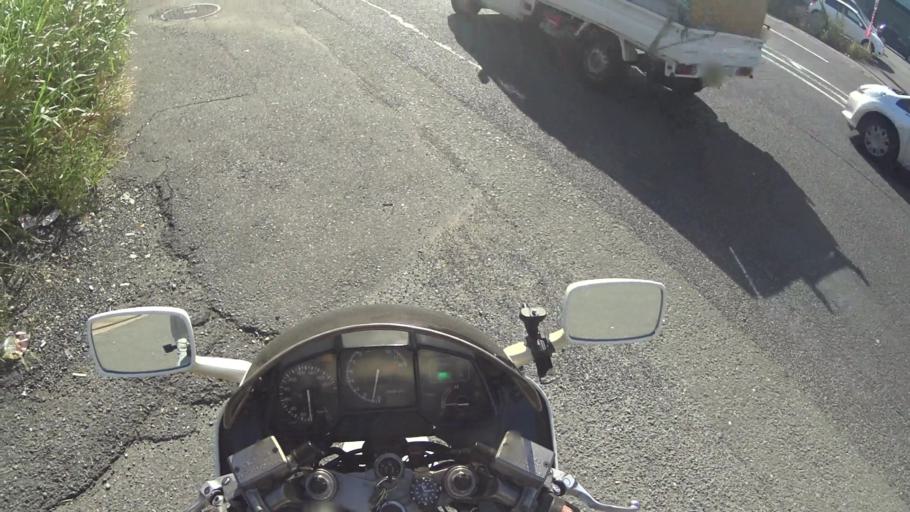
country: JP
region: Kyoto
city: Yawata
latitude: 34.8677
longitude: 135.7272
